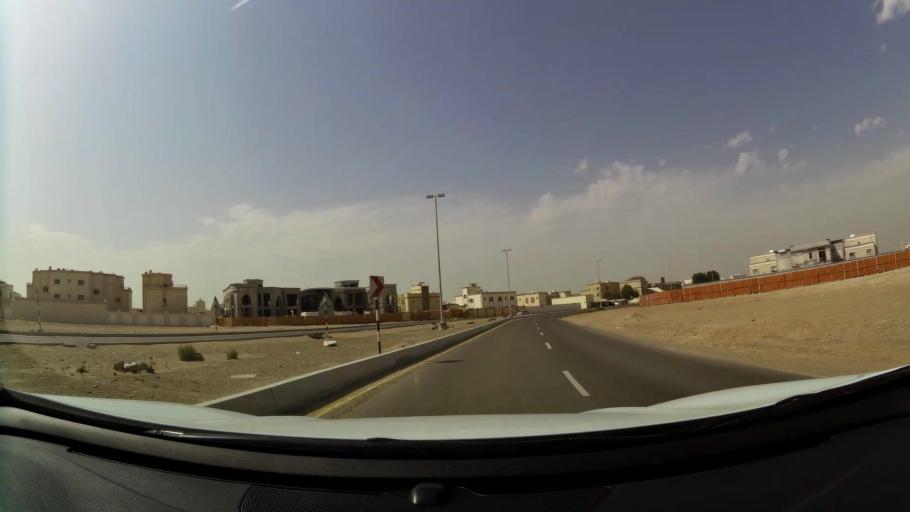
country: AE
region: Abu Dhabi
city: Abu Dhabi
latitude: 24.3323
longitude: 54.5496
